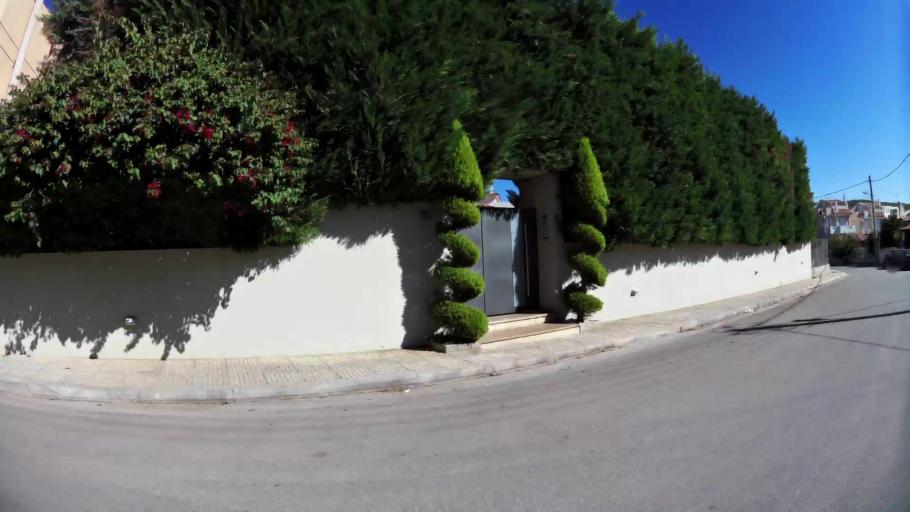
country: GR
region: Attica
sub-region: Nomarchia Anatolikis Attikis
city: Vari
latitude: 37.8374
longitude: 23.8161
